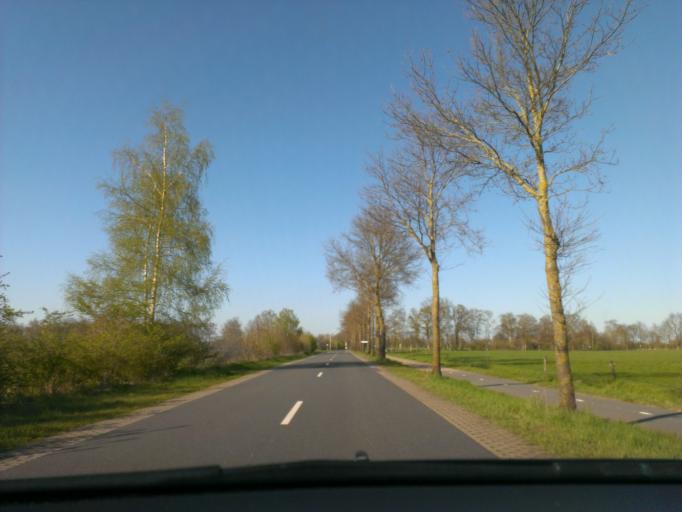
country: NL
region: Overijssel
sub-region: Gemeente Twenterand
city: Den Ham
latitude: 52.4409
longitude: 6.4752
